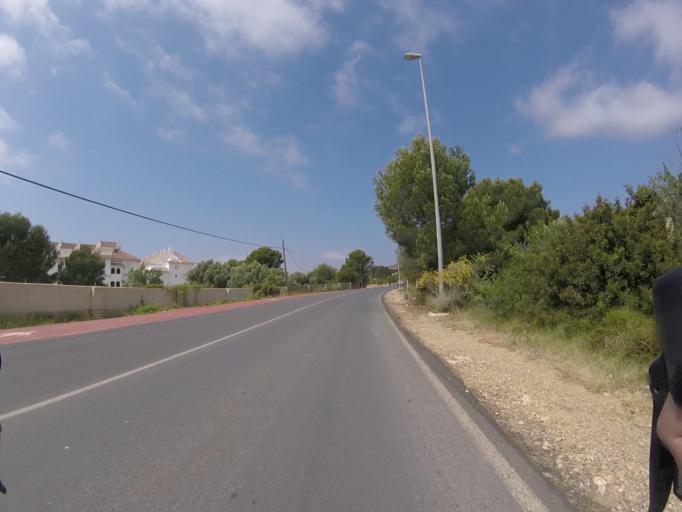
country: ES
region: Valencia
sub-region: Provincia de Castello
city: Alcoceber
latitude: 40.2509
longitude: 0.2795
